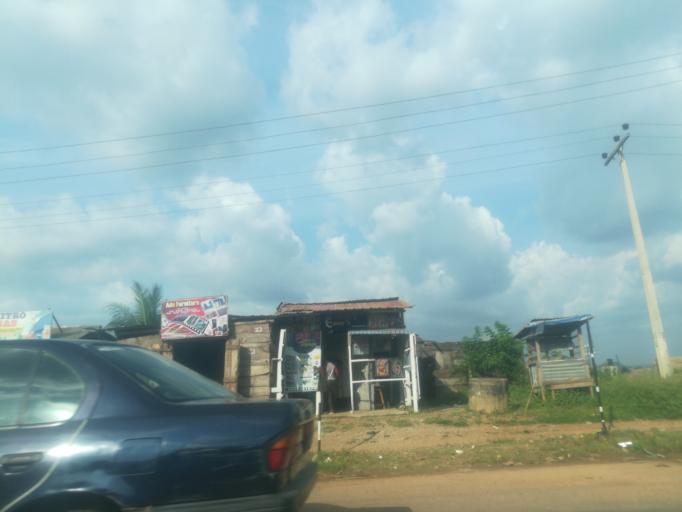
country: NG
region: Oyo
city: Ido
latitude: 7.3967
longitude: 3.8086
